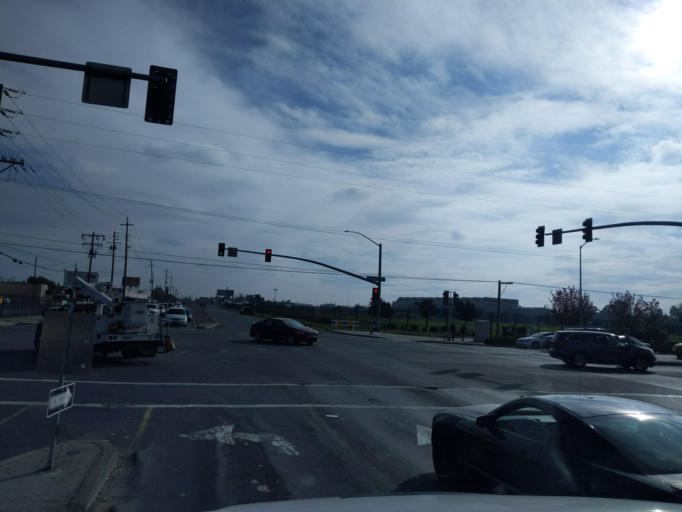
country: US
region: California
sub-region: San Joaquin County
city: August
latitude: 37.9842
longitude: -121.2840
